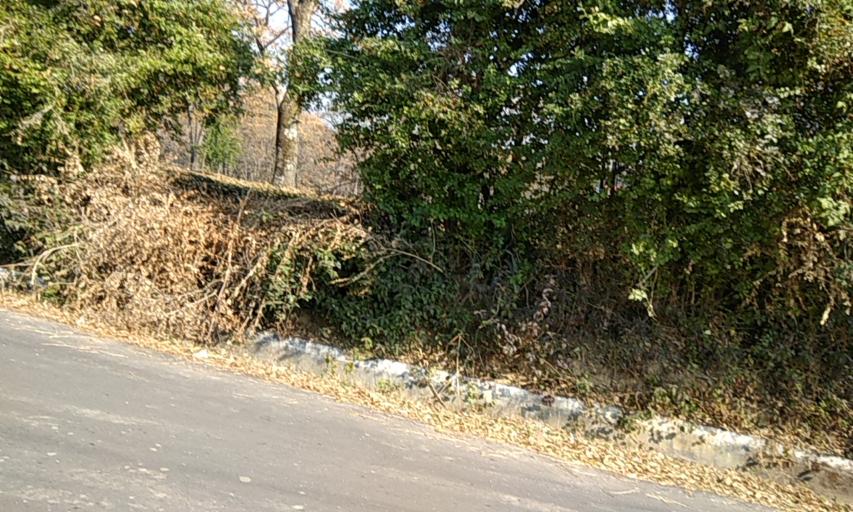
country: IN
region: Himachal Pradesh
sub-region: Kangra
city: Palampur
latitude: 32.1192
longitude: 76.5249
